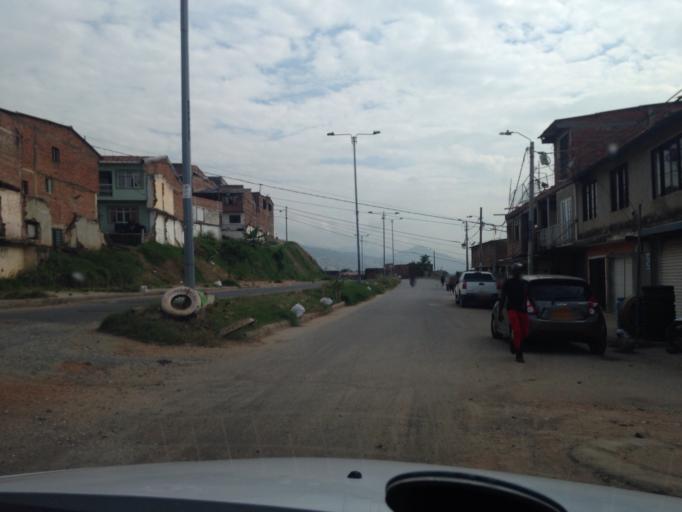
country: CO
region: Valle del Cauca
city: Cali
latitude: 3.3871
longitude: -76.5559
